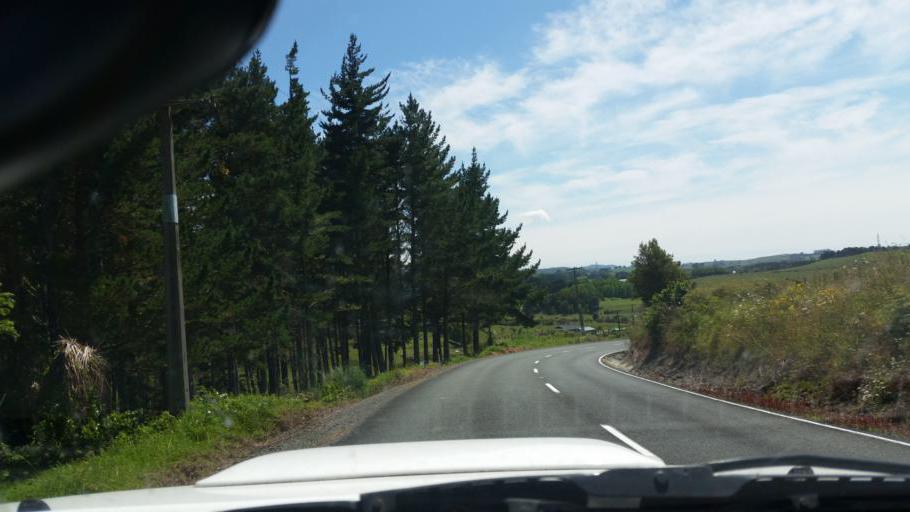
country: NZ
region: Auckland
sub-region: Auckland
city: Wellsford
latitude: -36.1716
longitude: 174.4182
